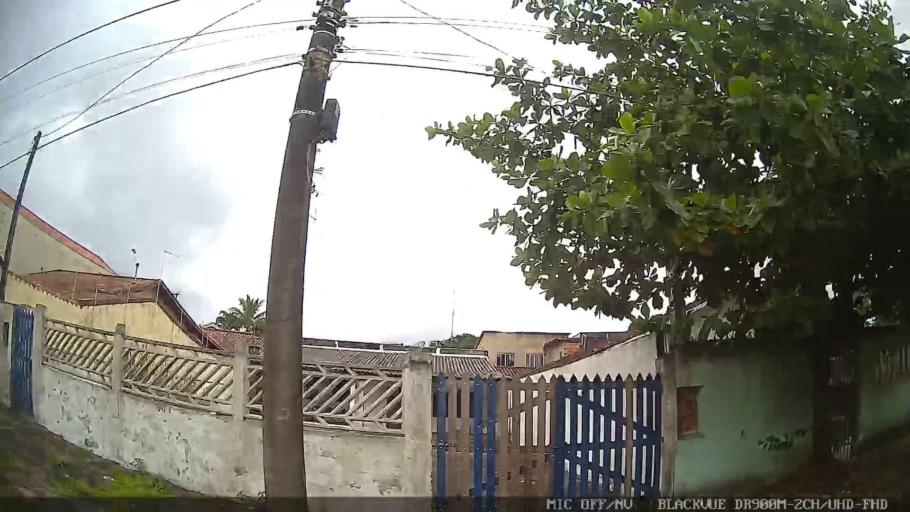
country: BR
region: Sao Paulo
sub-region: Itanhaem
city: Itanhaem
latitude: -24.1461
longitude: -46.7191
